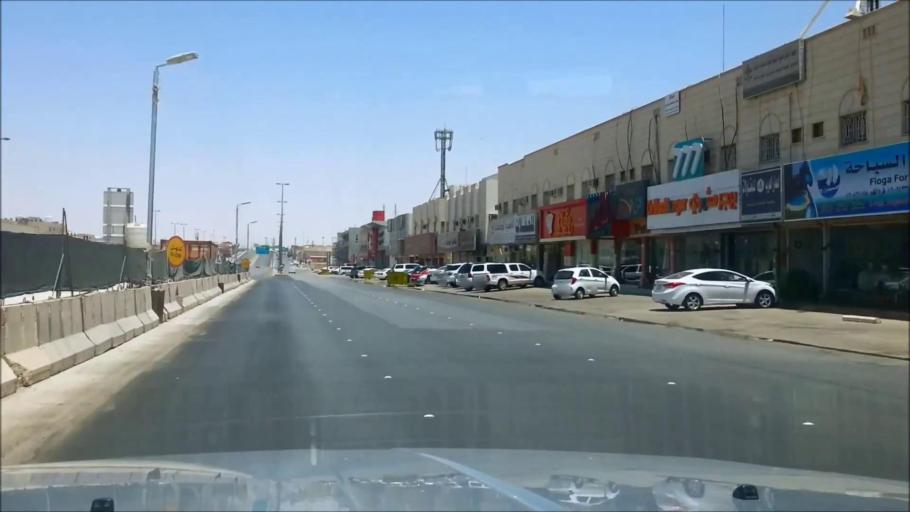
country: SA
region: Ar Riyad
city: Riyadh
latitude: 24.7562
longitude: 46.6755
